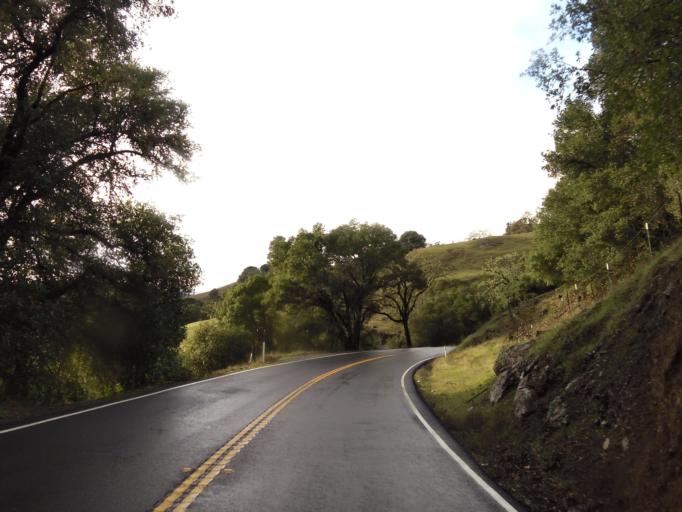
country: US
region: California
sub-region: Sonoma County
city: Cloverdale
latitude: 38.8855
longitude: -123.1288
